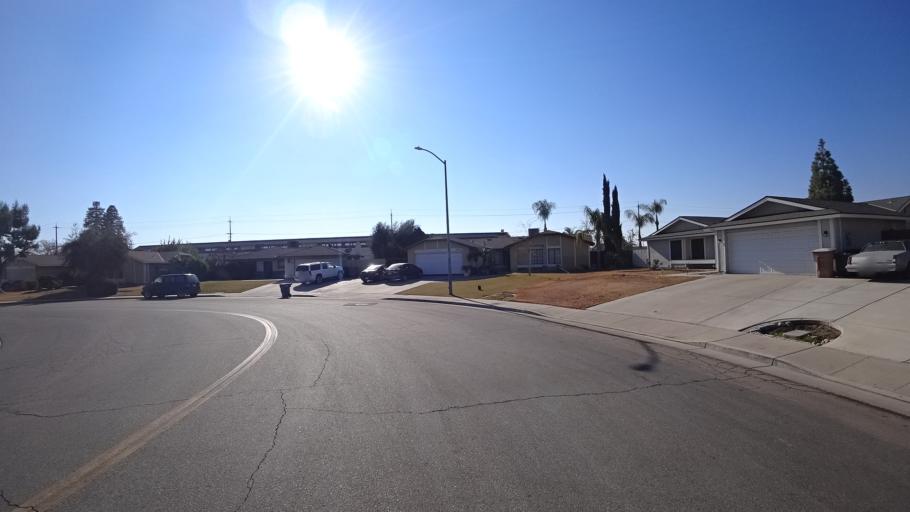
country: US
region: California
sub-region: Kern County
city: Greenfield
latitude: 35.2972
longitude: -119.0383
